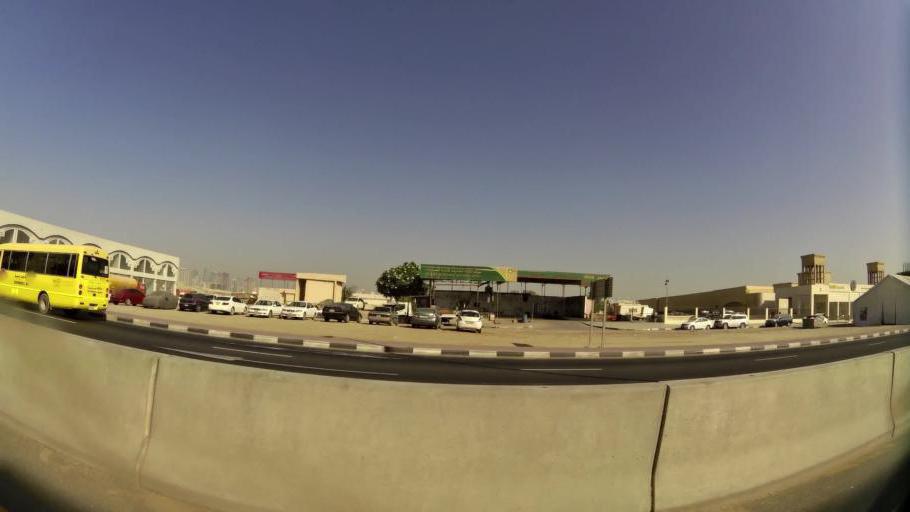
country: AE
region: Ash Shariqah
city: Sharjah
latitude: 25.3222
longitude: 55.4159
